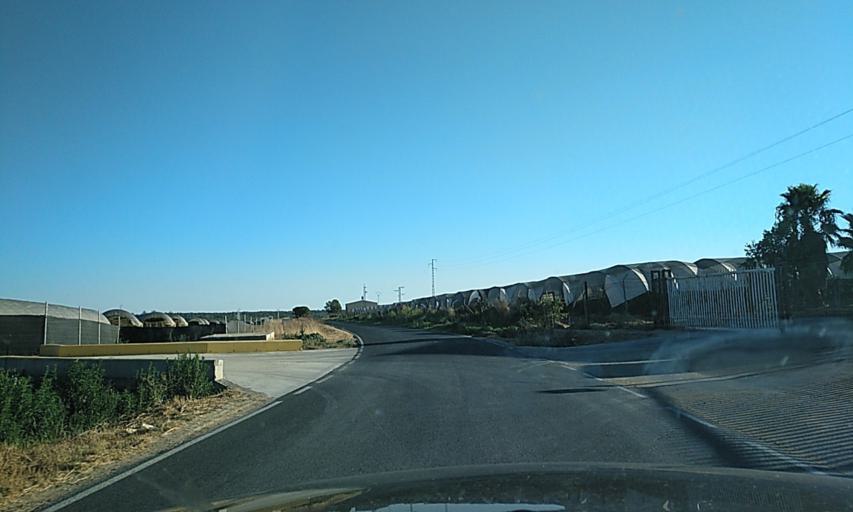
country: ES
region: Andalusia
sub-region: Provincia de Huelva
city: San Bartolome de la Torre
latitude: 37.4189
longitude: -7.1116
